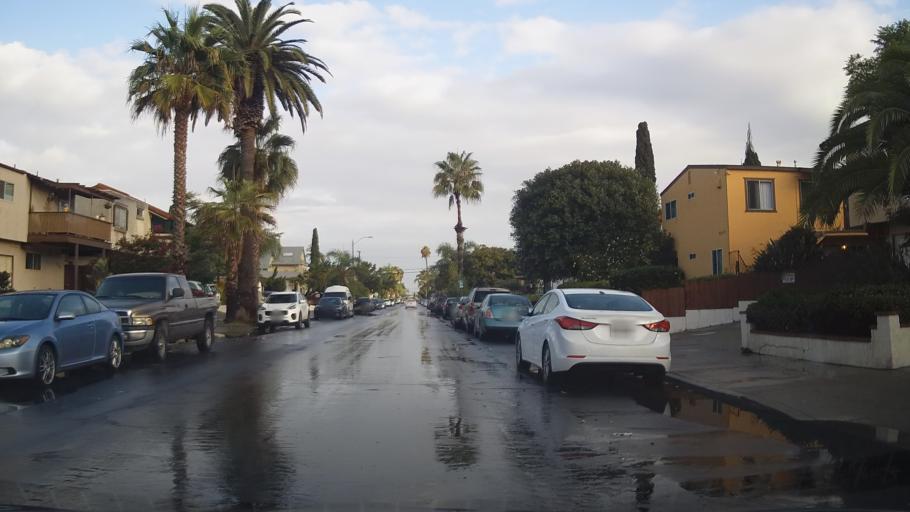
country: US
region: California
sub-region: San Diego County
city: San Diego
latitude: 32.7596
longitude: -117.1240
